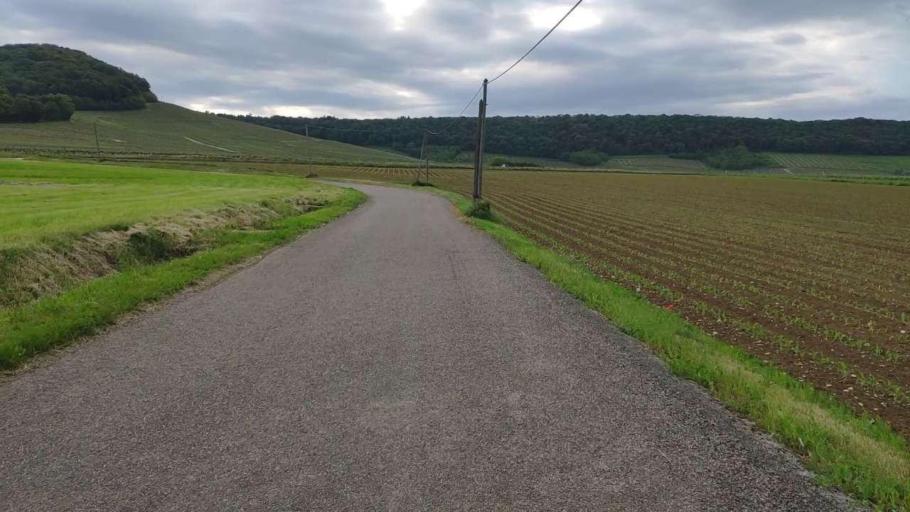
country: FR
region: Franche-Comte
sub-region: Departement du Jura
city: Perrigny
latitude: 46.7360
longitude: 5.5979
